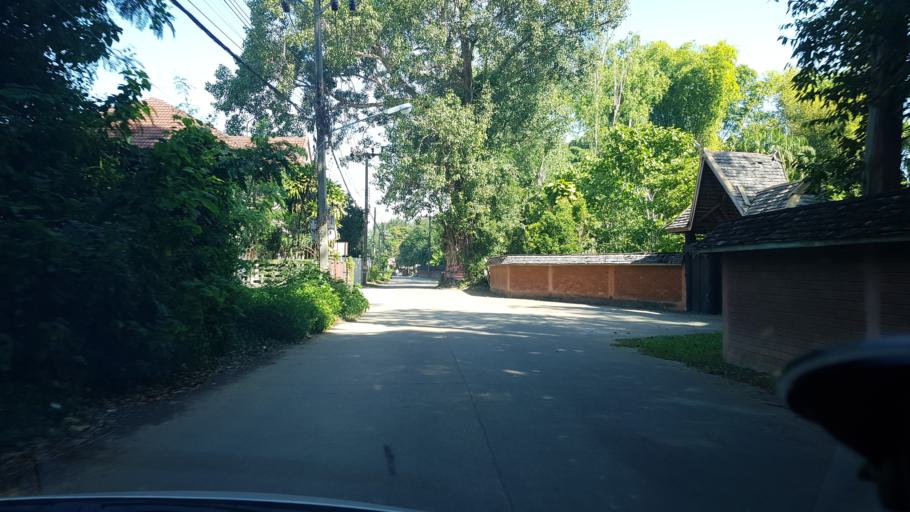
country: TH
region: Chiang Rai
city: Chiang Rai
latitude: 19.9049
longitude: 99.7932
